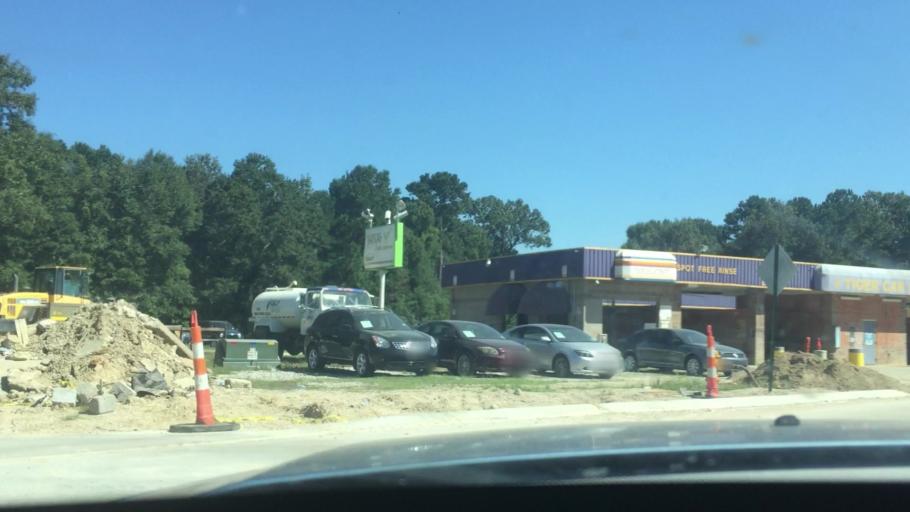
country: US
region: Louisiana
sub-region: East Baton Rouge Parish
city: Shenandoah
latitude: 30.4204
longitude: -91.0075
